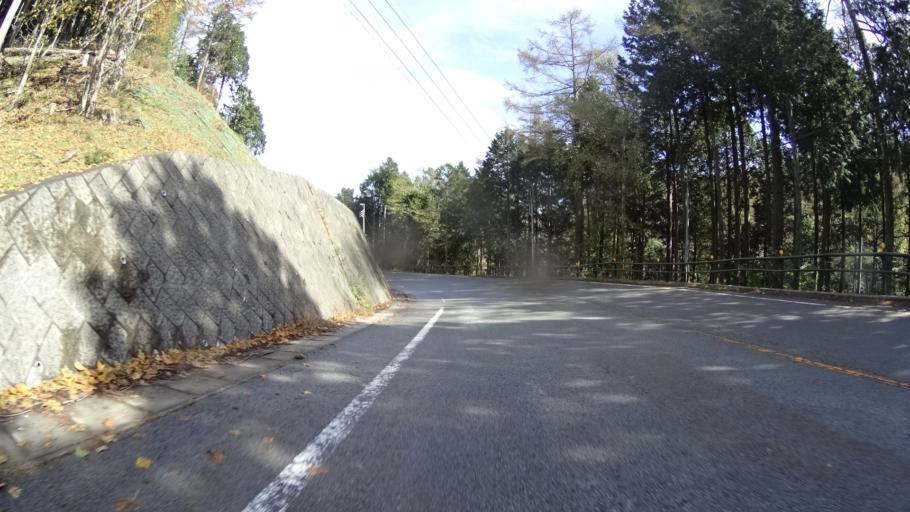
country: JP
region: Yamanashi
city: Enzan
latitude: 35.7920
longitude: 138.8045
